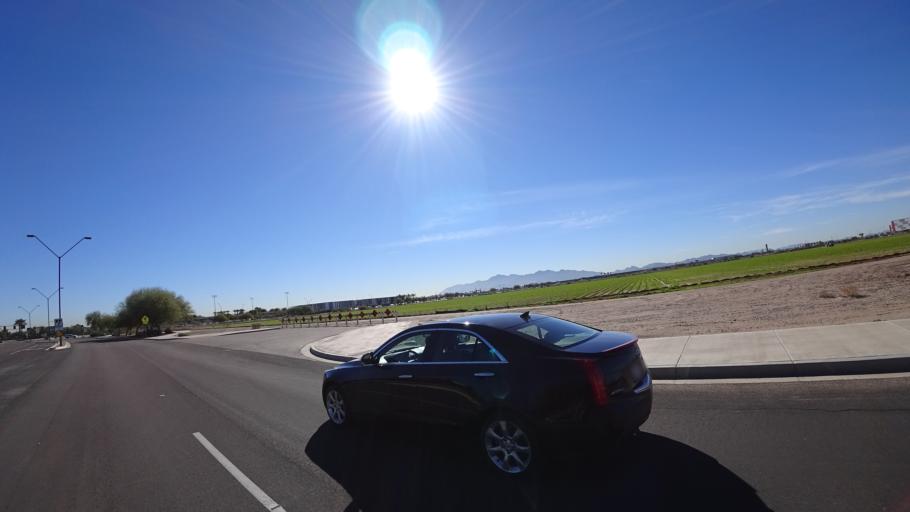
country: US
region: Arizona
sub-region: Maricopa County
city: Litchfield Park
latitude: 33.4718
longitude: -112.3778
